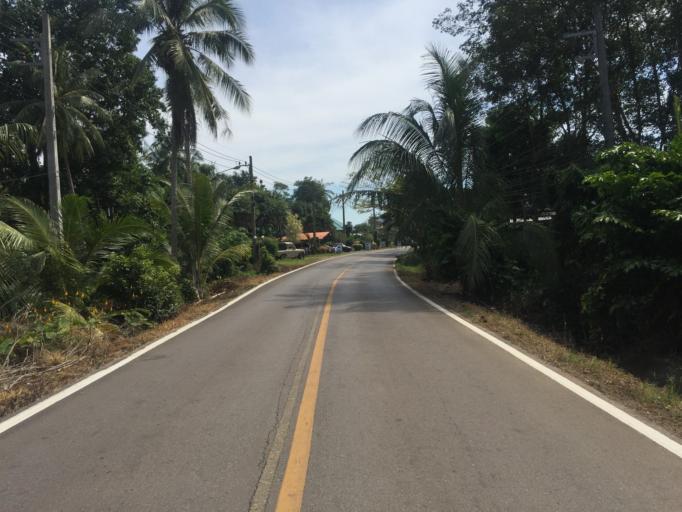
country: TH
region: Trat
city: Laem Ngop
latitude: 12.1284
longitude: 102.3248
